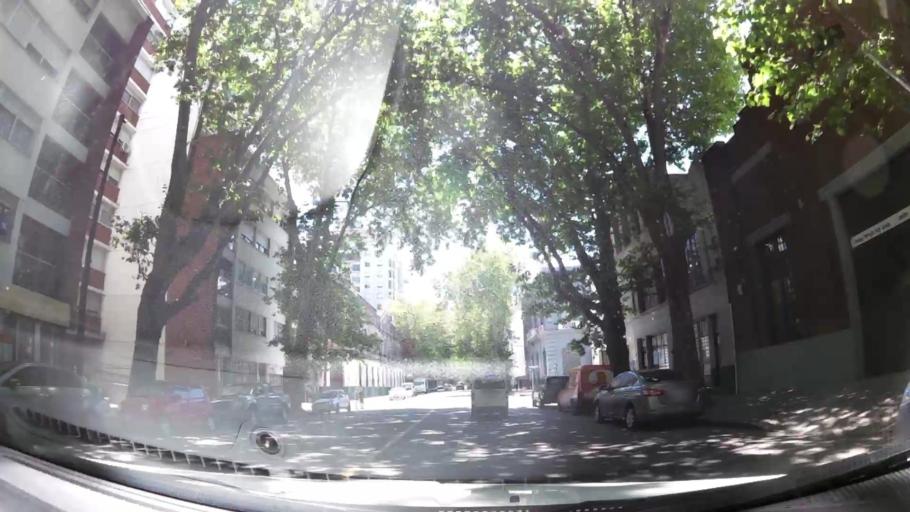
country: UY
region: Montevideo
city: Montevideo
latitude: -34.8973
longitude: -56.1923
